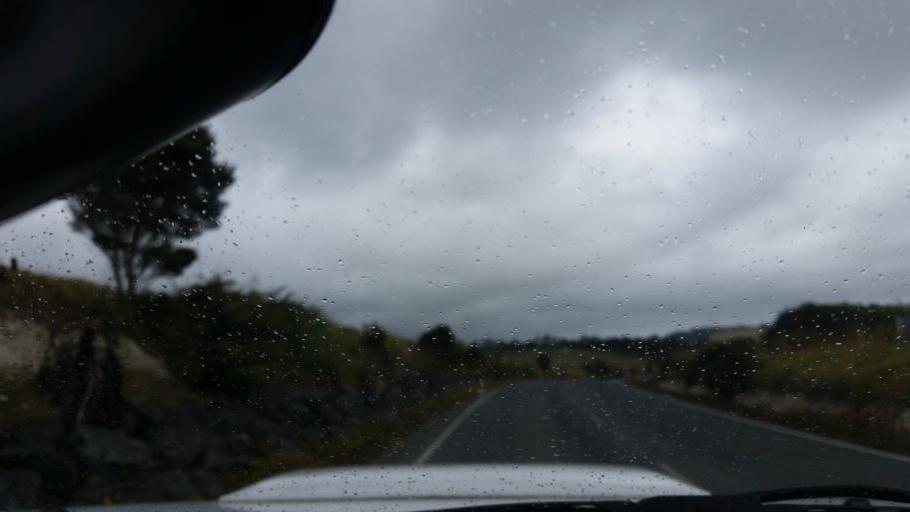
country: NZ
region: Auckland
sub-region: Auckland
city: Wellsford
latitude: -36.1427
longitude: 174.4990
